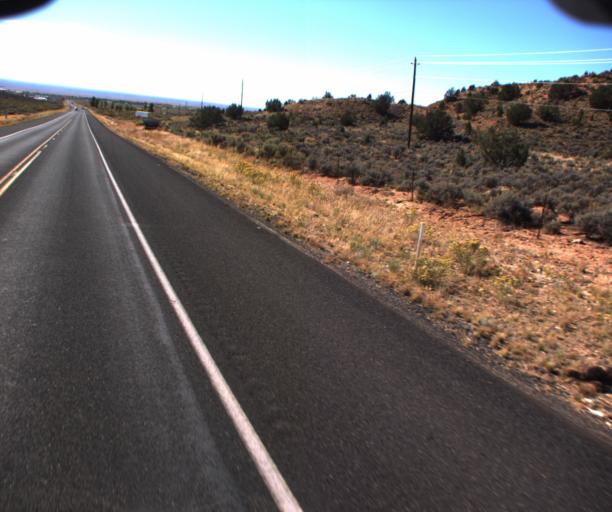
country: US
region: Arizona
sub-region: Coconino County
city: Fredonia
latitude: 36.9863
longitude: -112.5300
